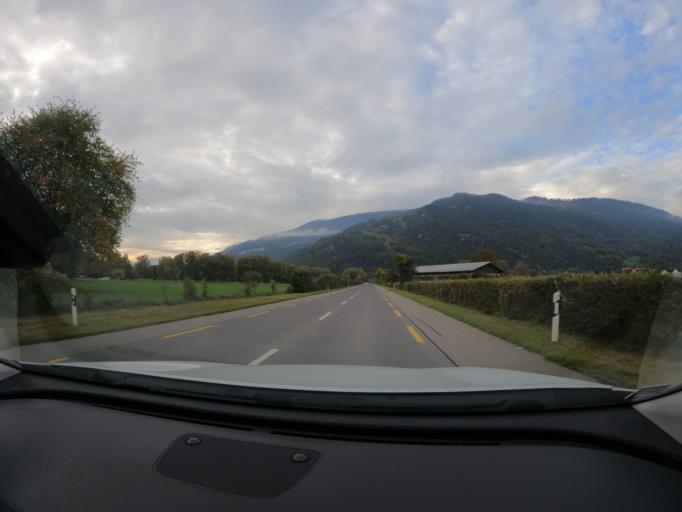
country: CH
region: Bern
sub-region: Interlaken-Oberhasli District
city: Unterseen
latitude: 46.6761
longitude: 7.8311
